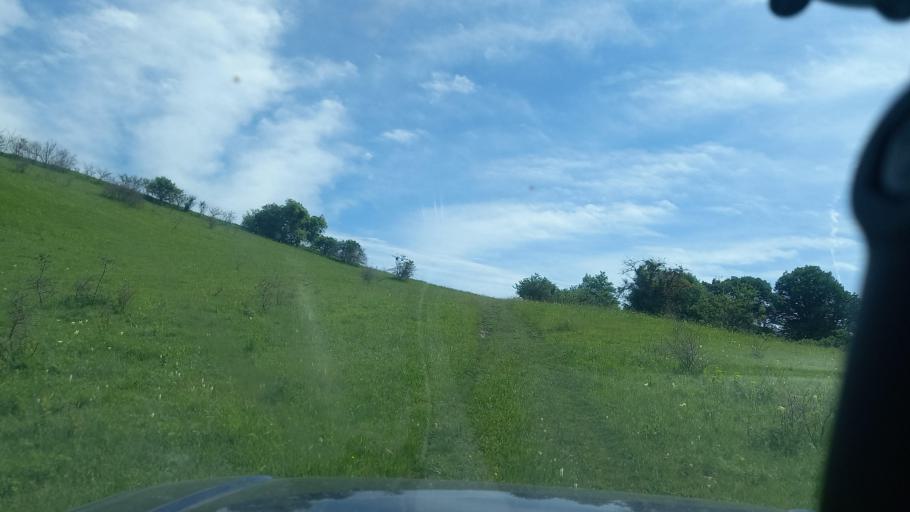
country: RU
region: Karachayevo-Cherkesiya
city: Kurdzhinovo
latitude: 44.1454
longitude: 41.0650
